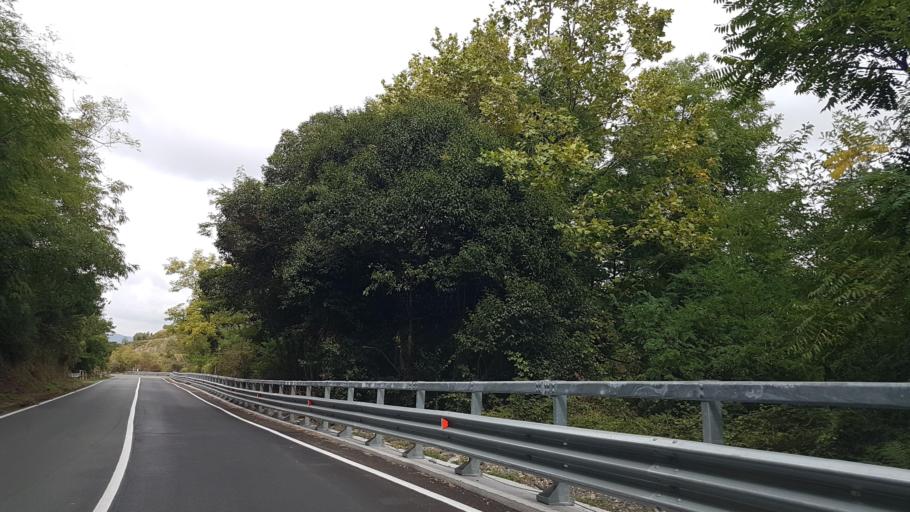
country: IT
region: Liguria
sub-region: Provincia di Genova
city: Moneglia
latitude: 44.2572
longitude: 9.4736
